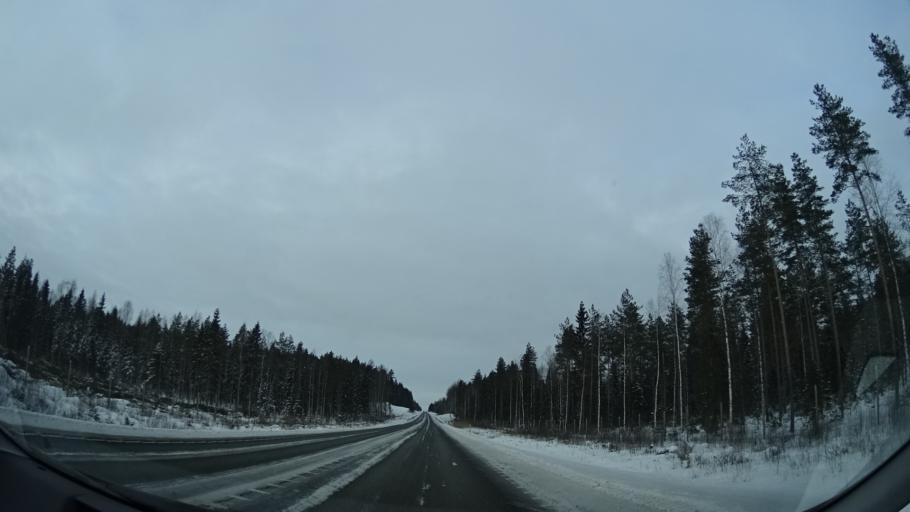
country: FI
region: Uusimaa
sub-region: Helsinki
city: Kaerkoelae
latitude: 60.6227
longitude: 23.9866
